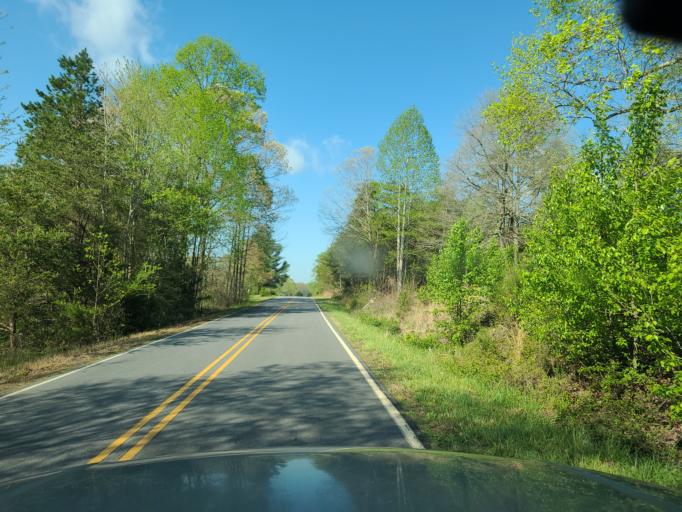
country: US
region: North Carolina
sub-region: Rutherford County
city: Spindale
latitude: 35.3969
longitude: -81.9055
